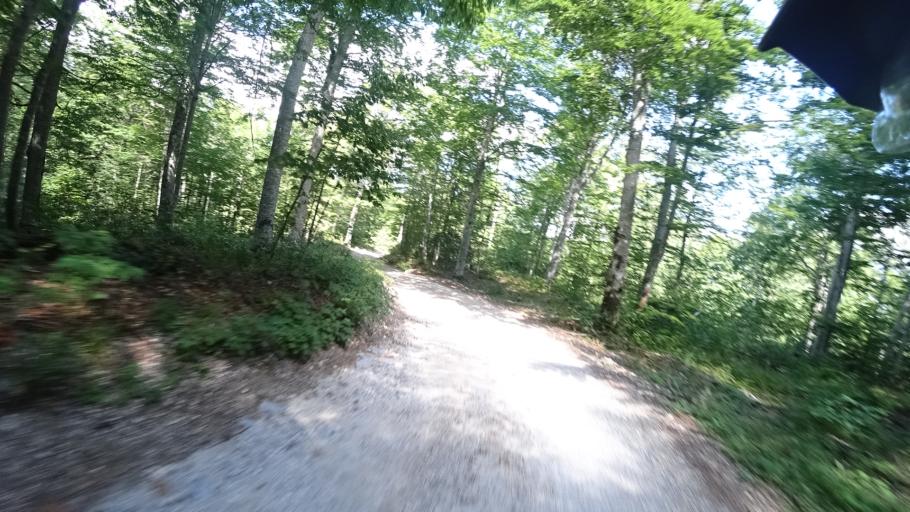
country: BA
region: Federation of Bosnia and Herzegovina
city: Orasac
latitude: 44.5006
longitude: 15.9482
